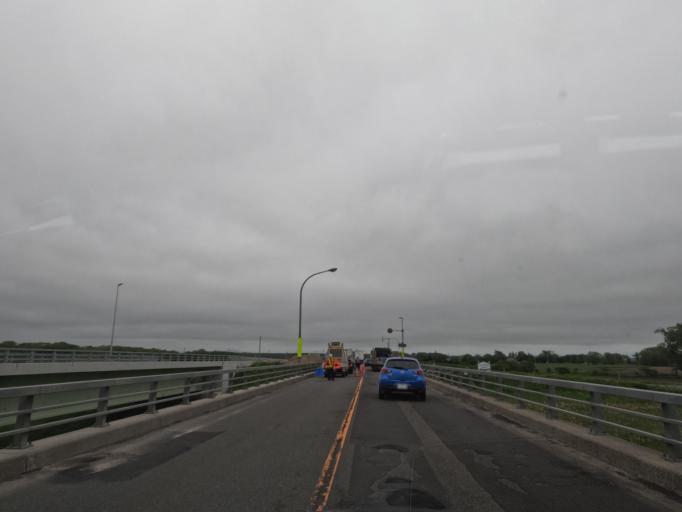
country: JP
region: Hokkaido
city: Ebetsu
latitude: 43.1385
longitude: 141.5126
